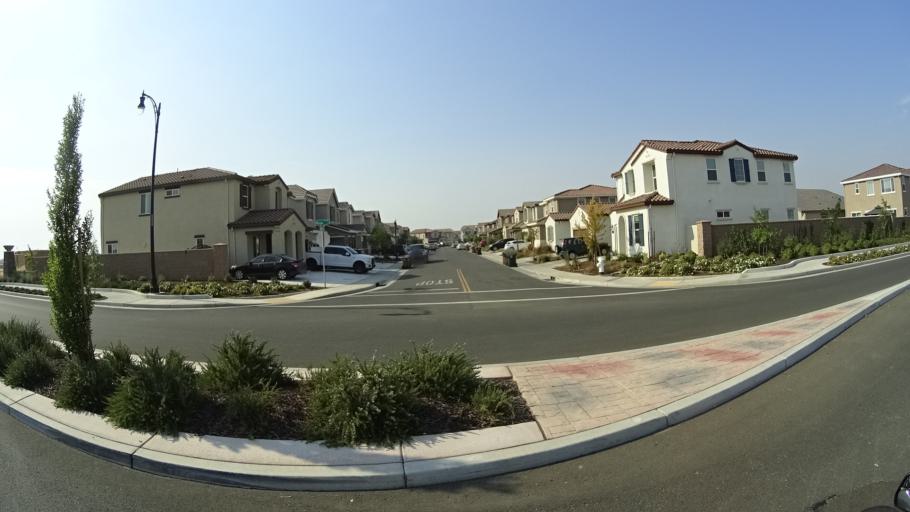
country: US
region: California
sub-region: Sacramento County
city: Elk Grove
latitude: 38.3839
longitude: -121.3754
